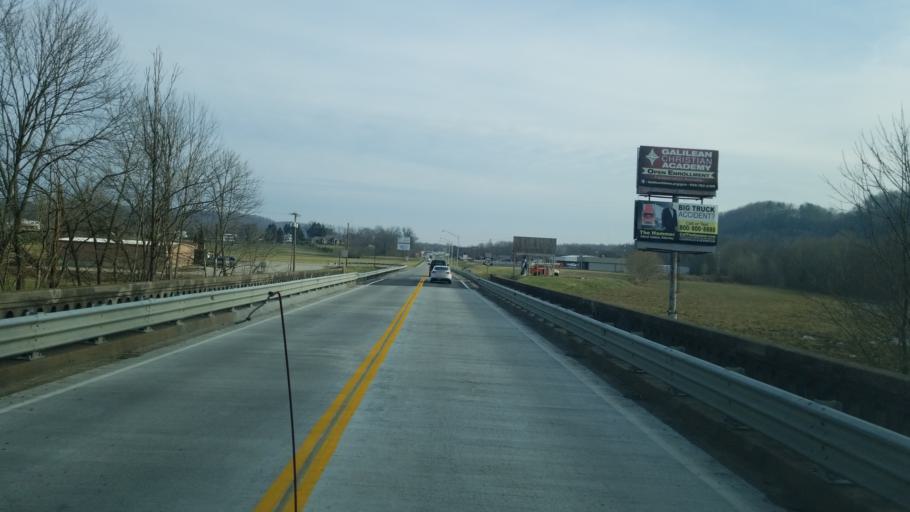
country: US
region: Kentucky
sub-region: Casey County
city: Liberty
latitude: 37.3104
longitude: -84.9402
